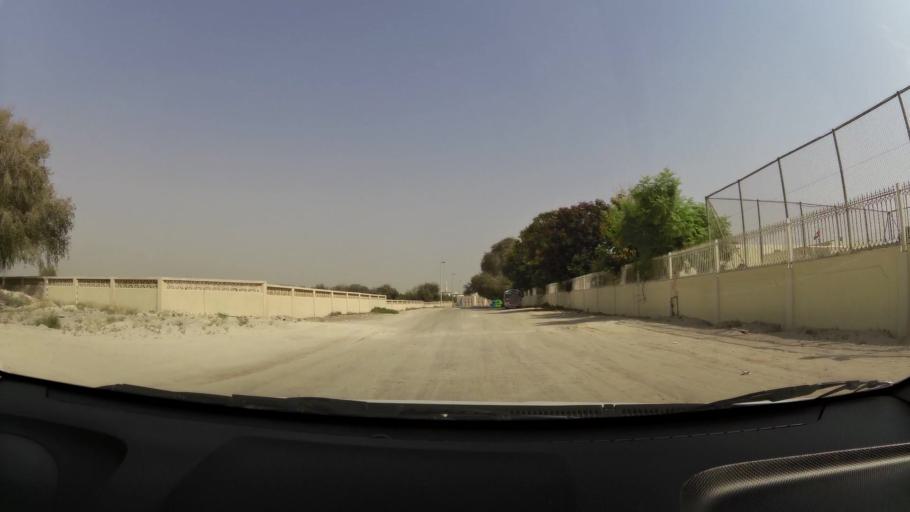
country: AE
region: Ajman
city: Ajman
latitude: 25.3844
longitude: 55.4178
